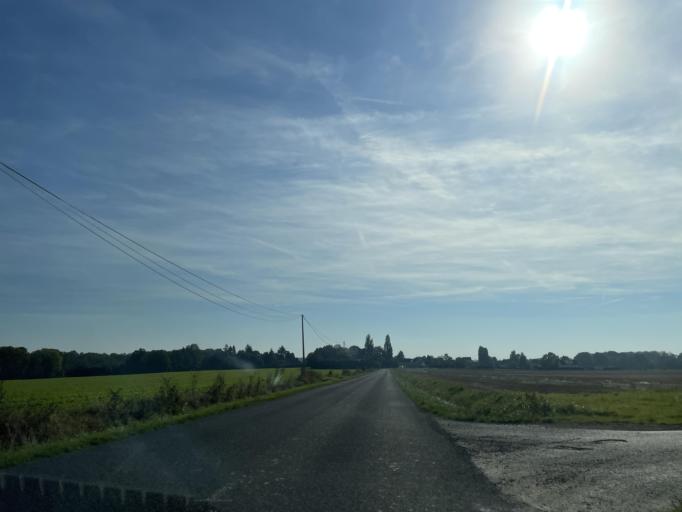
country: FR
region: Ile-de-France
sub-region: Departement de Seine-et-Marne
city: Saint-Jean-les-Deux-Jumeaux
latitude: 48.9035
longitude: 3.0315
